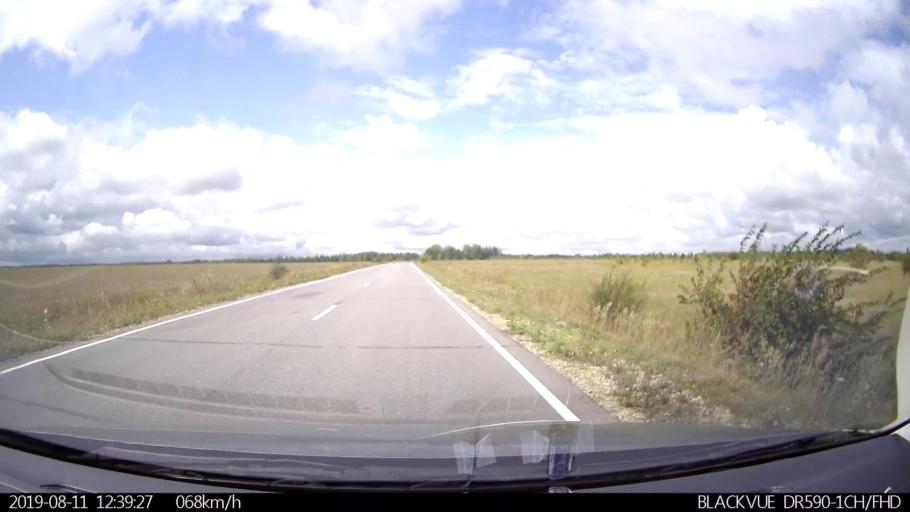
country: RU
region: Ulyanovsk
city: Ignatovka
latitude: 53.8333
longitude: 47.7954
